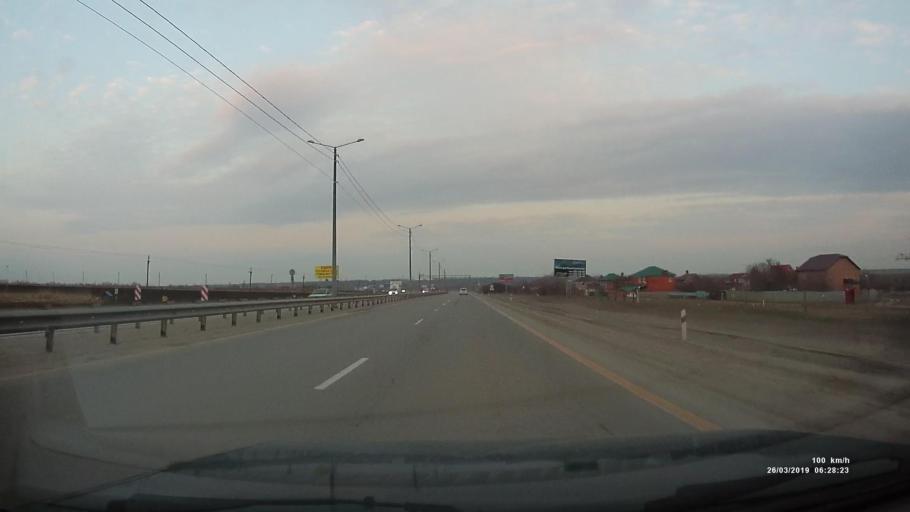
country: RU
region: Rostov
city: Krym
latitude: 47.2653
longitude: 39.5941
